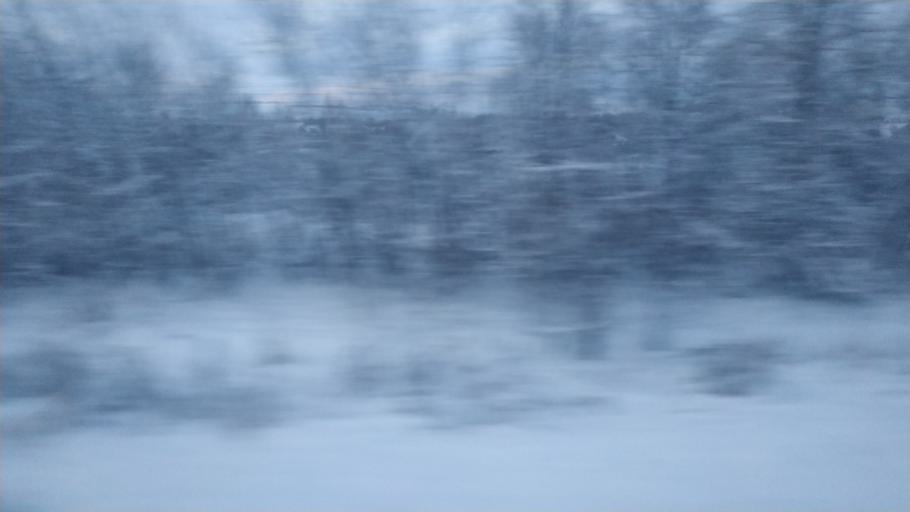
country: RU
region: Tatarstan
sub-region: Arskiy Rayon
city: Arsk
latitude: 56.0220
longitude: 49.6451
